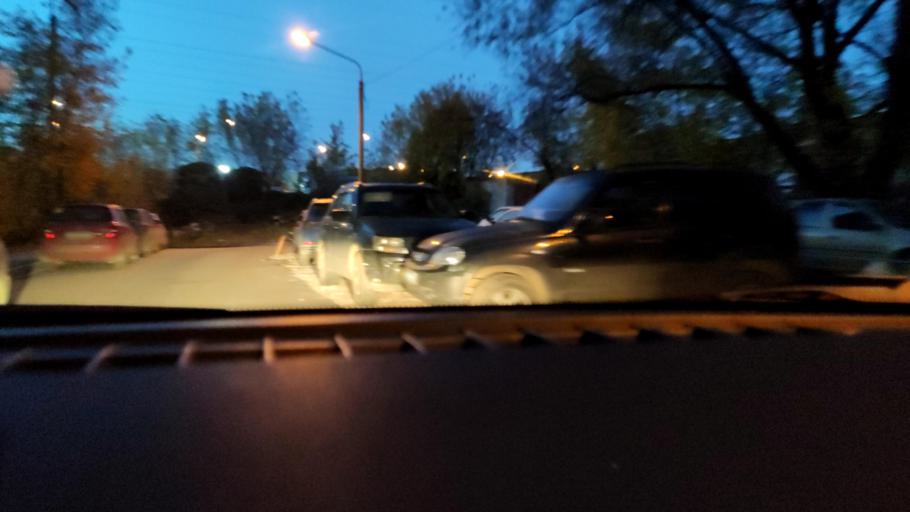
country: RU
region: Perm
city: Perm
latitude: 57.9878
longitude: 56.2748
